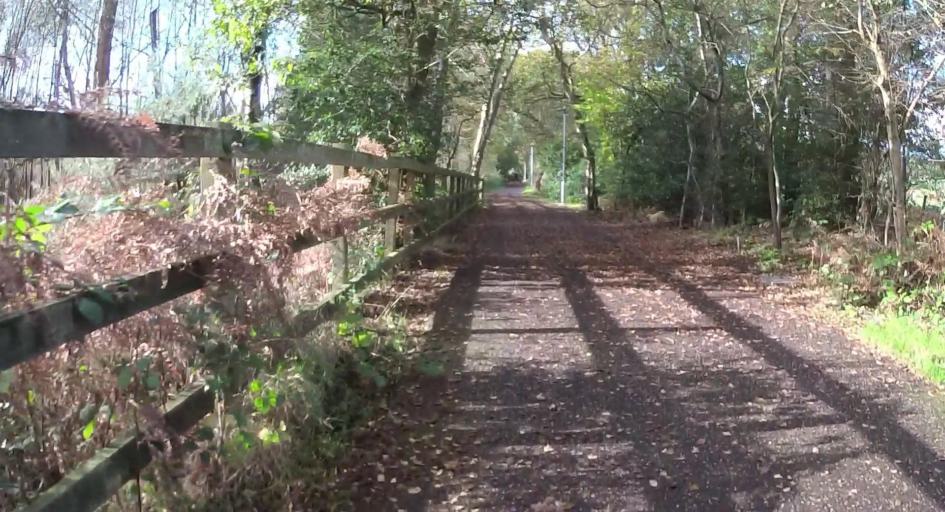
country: GB
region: England
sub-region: Wokingham
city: Barkham
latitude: 51.3831
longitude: -0.8783
